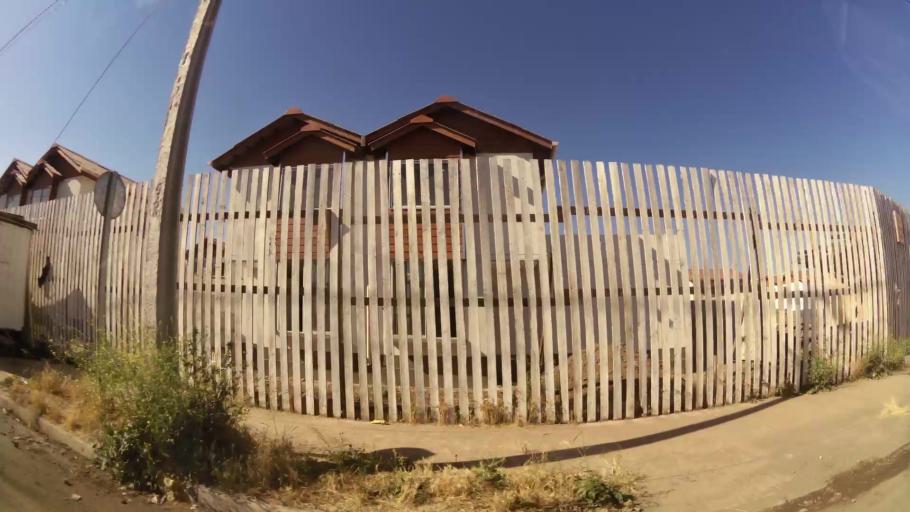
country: CL
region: Santiago Metropolitan
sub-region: Provincia de Maipo
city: San Bernardo
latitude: -33.6080
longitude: -70.6826
